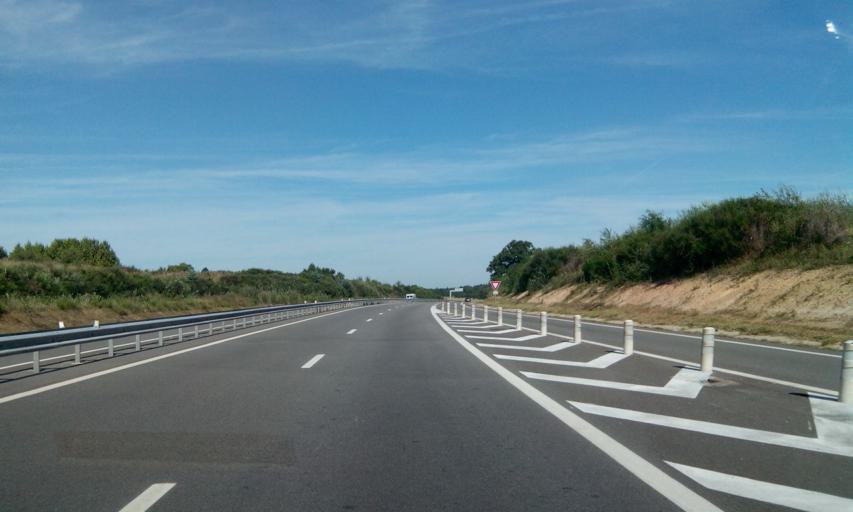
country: FR
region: Limousin
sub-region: Departement de la Haute-Vienne
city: Verneuil-sur-Vienne
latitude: 45.8595
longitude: 1.1433
